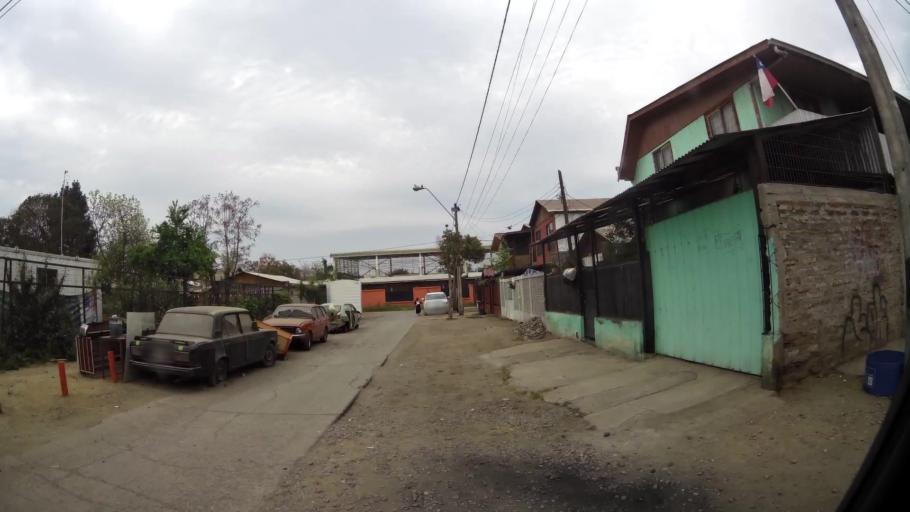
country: CL
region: Santiago Metropolitan
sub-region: Provincia de Santiago
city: Lo Prado
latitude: -33.4978
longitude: -70.7663
